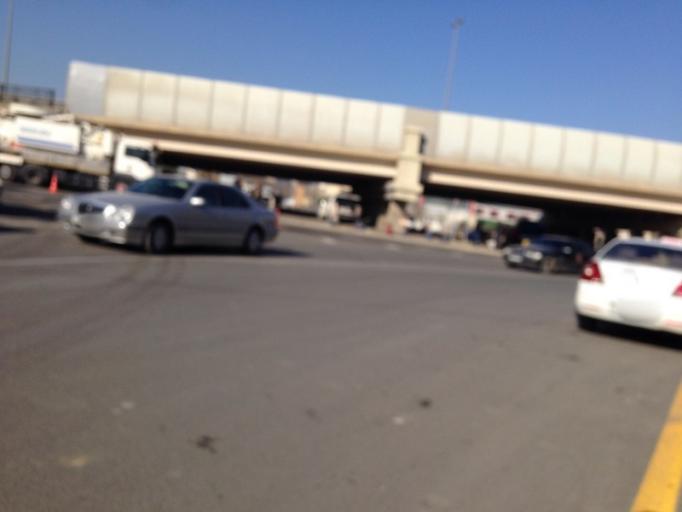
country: AZ
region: Baki
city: Baku
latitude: 40.4188
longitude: 49.8664
